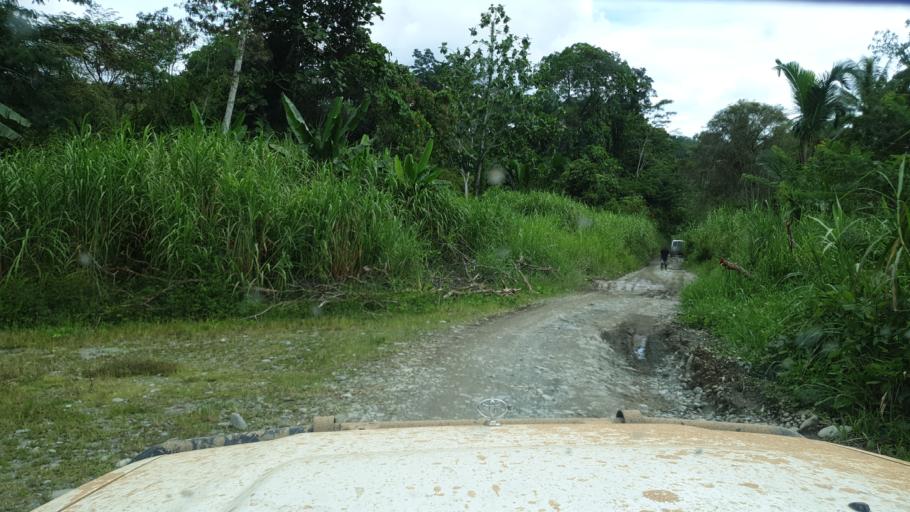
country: PG
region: Northern Province
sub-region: Sohe
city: Kokoda
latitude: -8.9160
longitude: 147.8726
